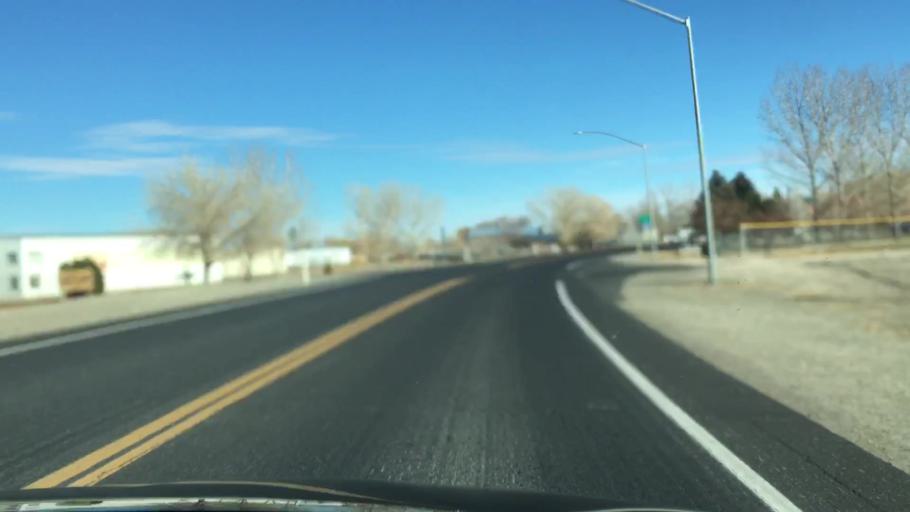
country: US
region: Nevada
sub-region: Lyon County
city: Yerington
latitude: 38.9971
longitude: -119.1605
